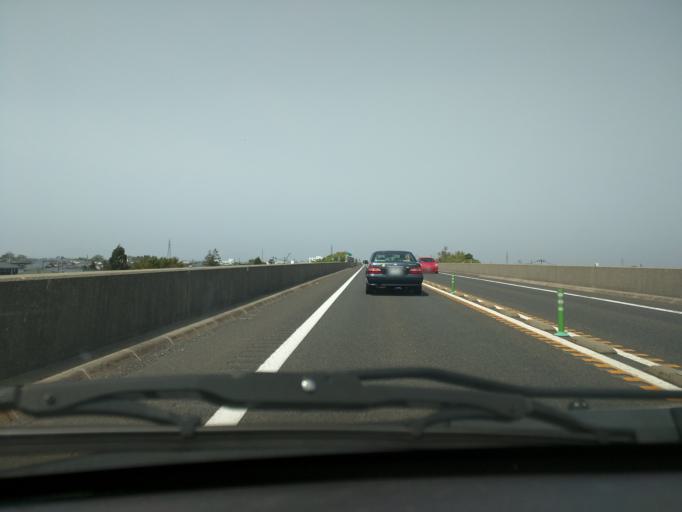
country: JP
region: Niigata
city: Niitsu-honcho
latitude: 37.8197
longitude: 139.1212
